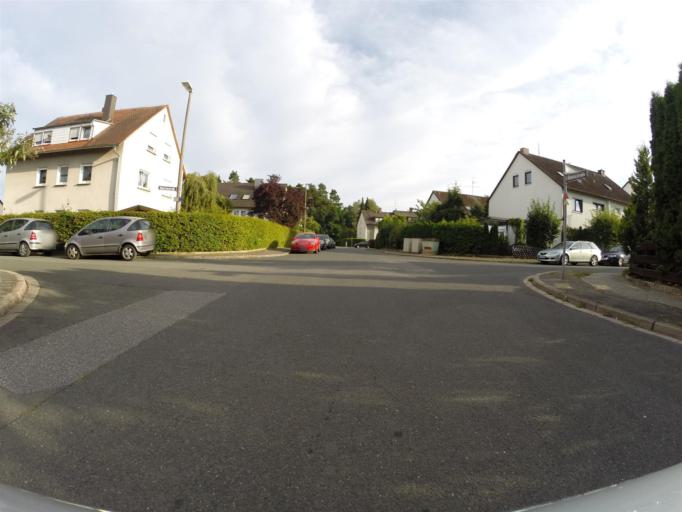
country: DE
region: Bavaria
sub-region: Regierungsbezirk Mittelfranken
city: Stein
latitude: 49.3985
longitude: 11.0203
